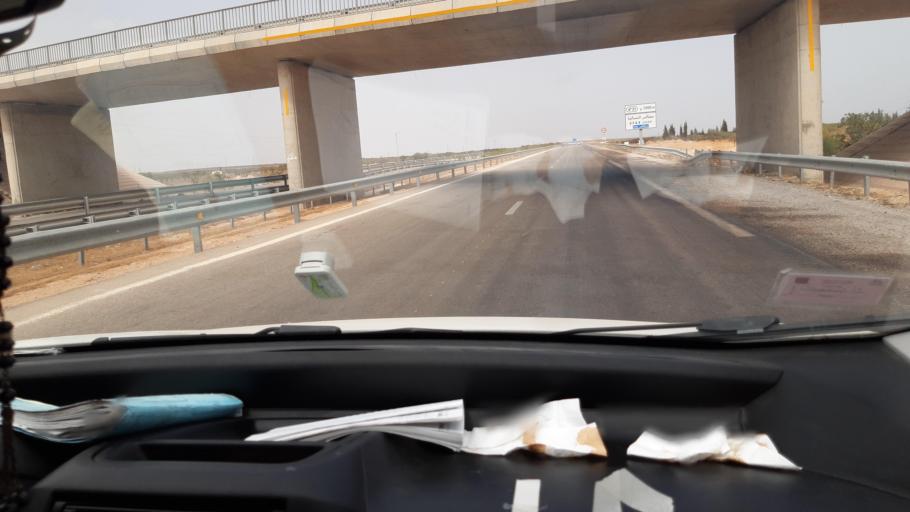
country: TN
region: Safaqis
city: Sfax
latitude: 34.8833
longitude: 10.7069
